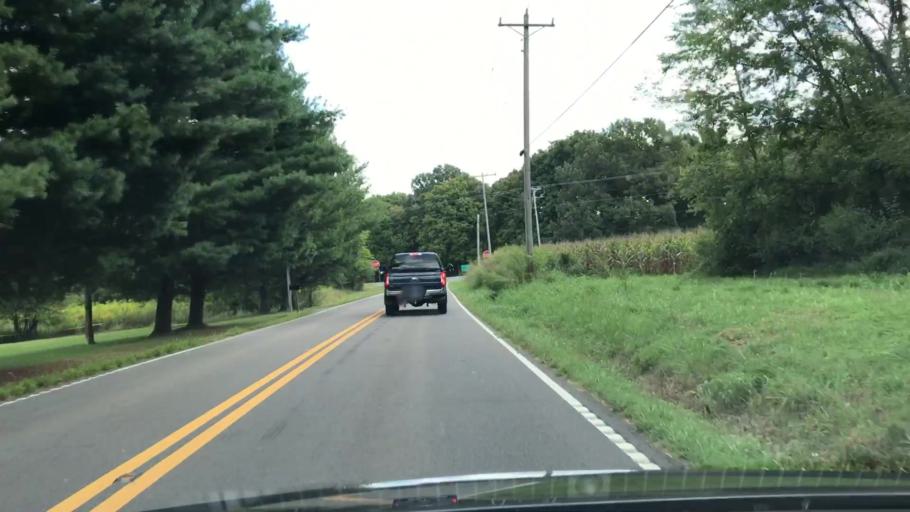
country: US
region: Tennessee
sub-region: Robertson County
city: Springfield
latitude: 36.5541
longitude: -86.8137
